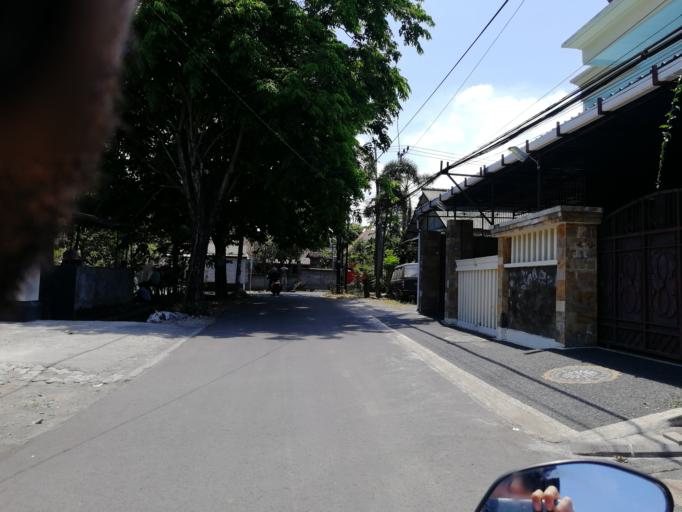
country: ID
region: Bali
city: Dajan Tangluk
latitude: -8.6650
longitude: 115.2339
